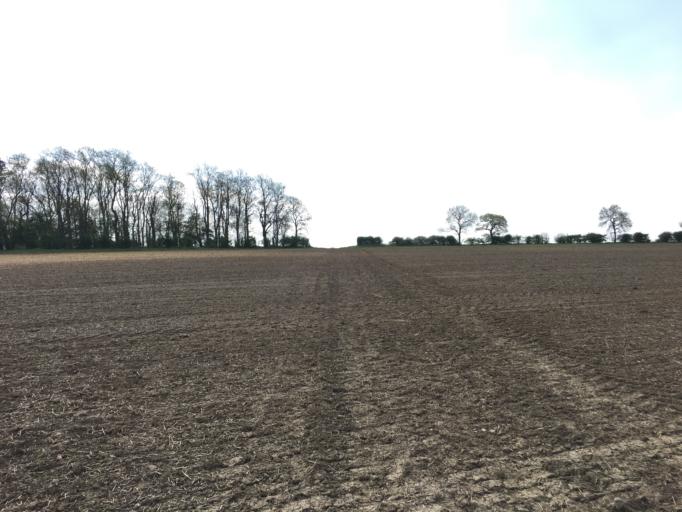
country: GB
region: England
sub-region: Leicestershire
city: Houghton on the Hill
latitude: 52.6107
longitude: -0.9950
